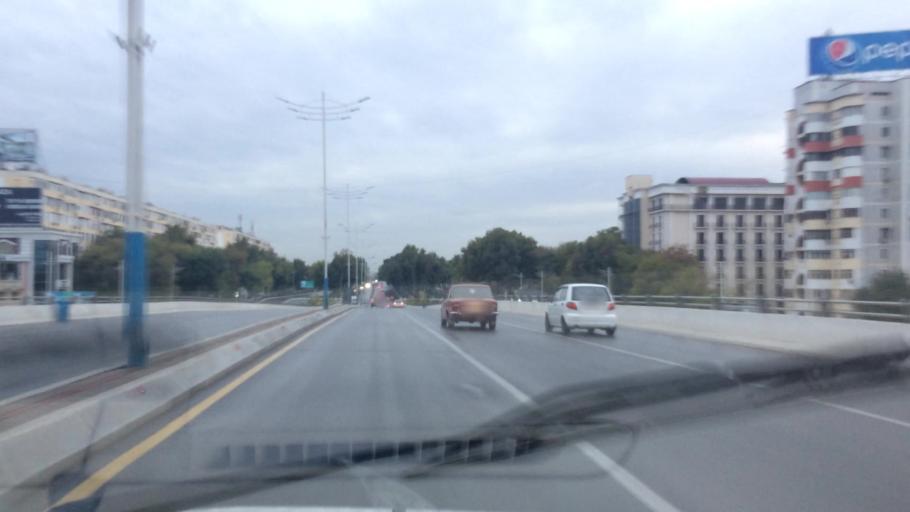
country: UZ
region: Toshkent Shahri
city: Tashkent
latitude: 41.2919
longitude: 69.2231
